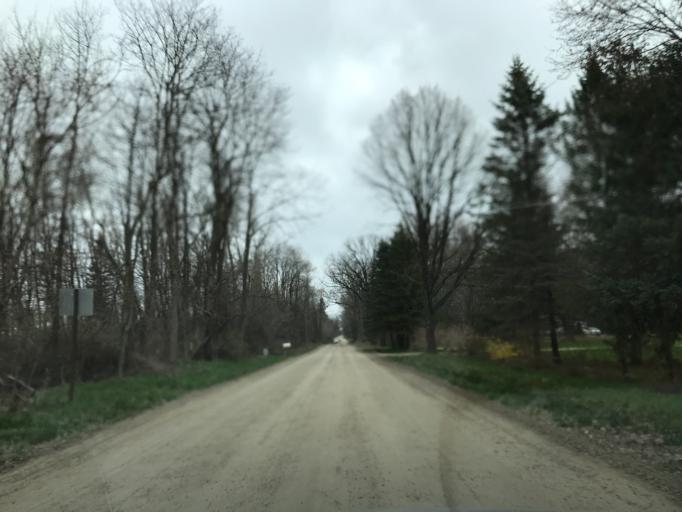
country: US
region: Michigan
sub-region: Oakland County
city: South Lyon
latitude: 42.4834
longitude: -83.6682
